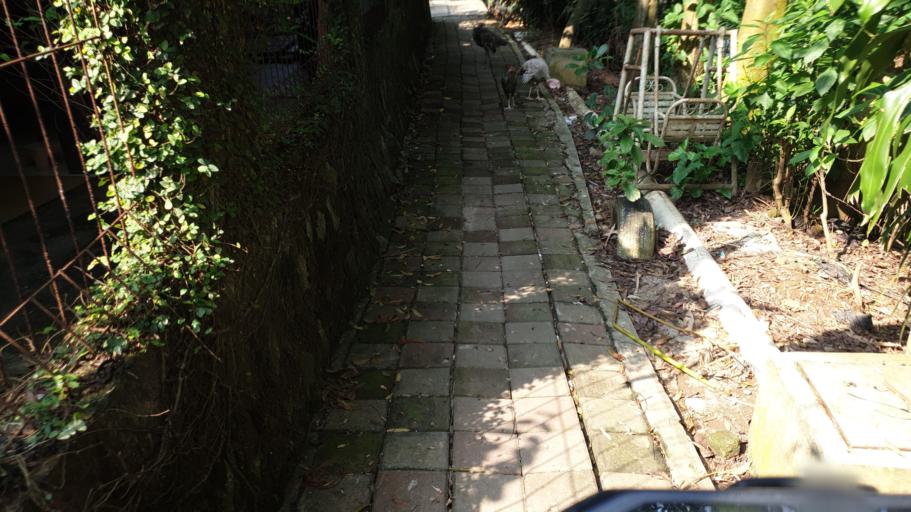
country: ID
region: West Java
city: Depok
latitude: -6.3689
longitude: 106.8402
